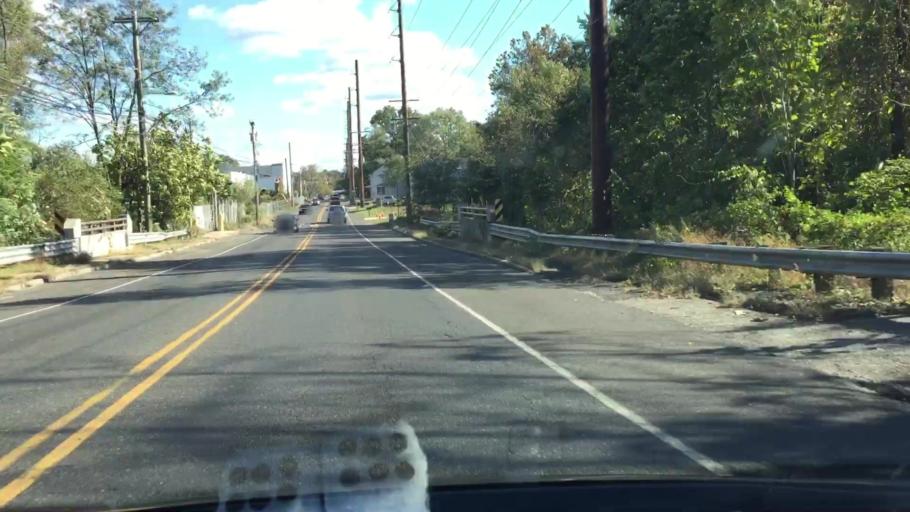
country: US
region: New Jersey
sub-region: Gloucester County
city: Turnersville
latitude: 39.7750
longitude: -75.0544
